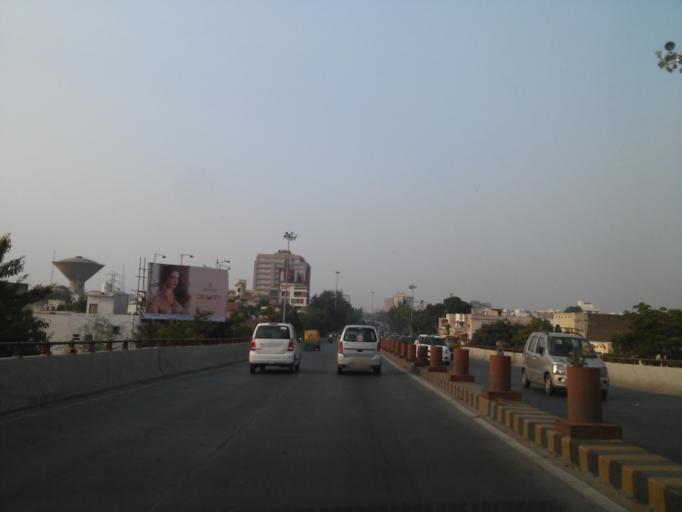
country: IN
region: Gujarat
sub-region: Ahmadabad
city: Ahmedabad
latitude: 23.0134
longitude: 72.5452
